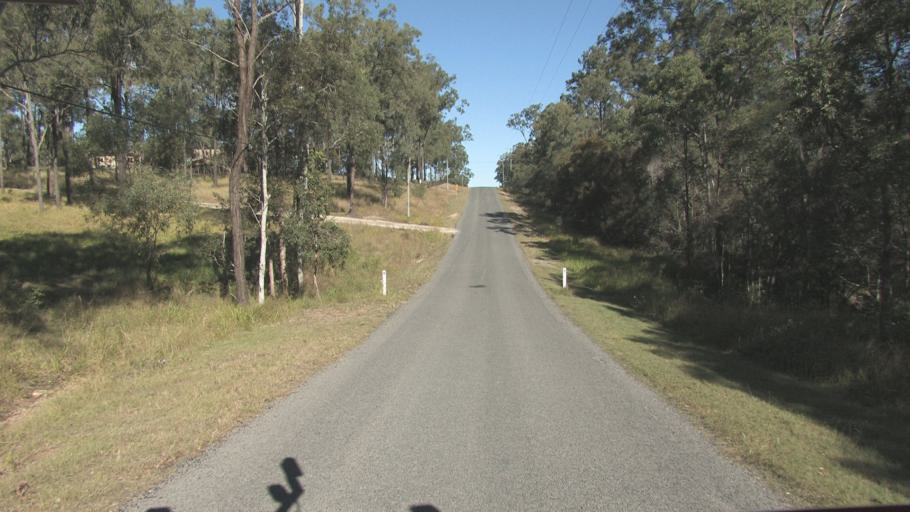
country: AU
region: Queensland
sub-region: Logan
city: Chambers Flat
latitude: -27.8136
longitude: 153.0779
